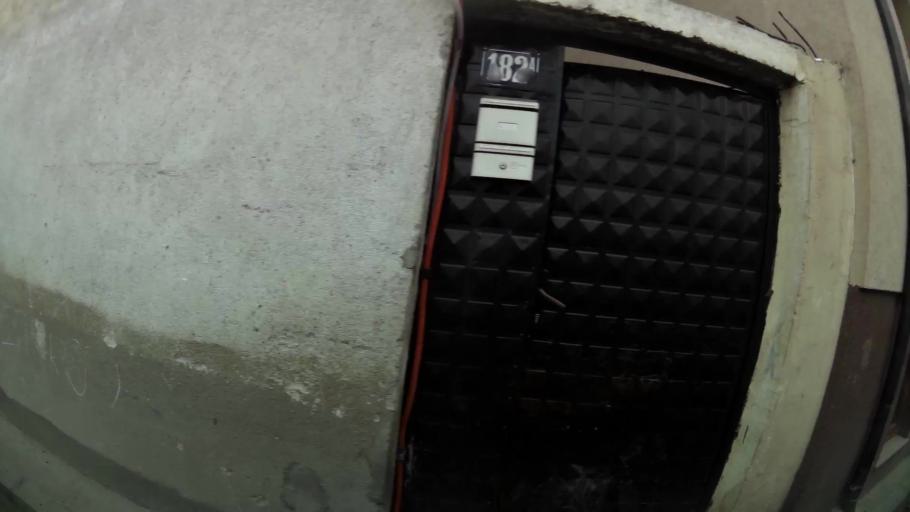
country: MK
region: Cair
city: Cair
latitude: 42.0085
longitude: 21.4454
